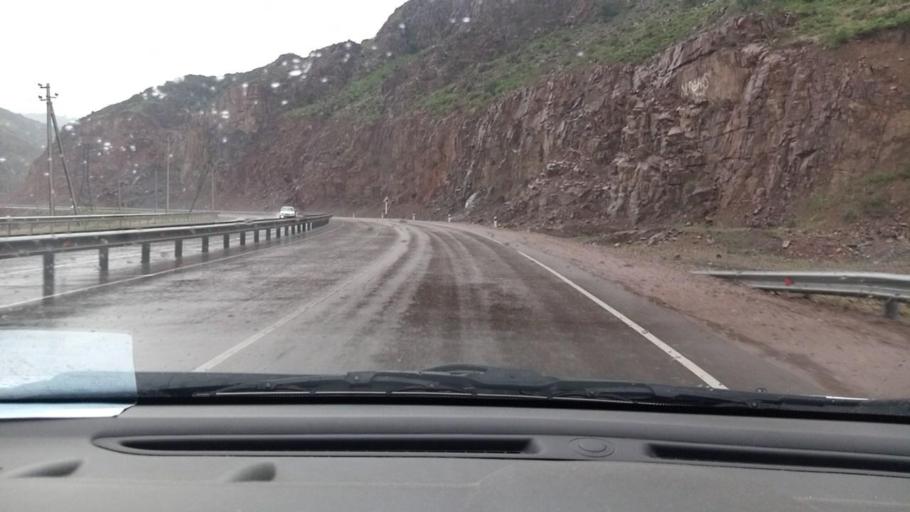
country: UZ
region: Toshkent
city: Angren
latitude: 41.0818
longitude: 70.3226
